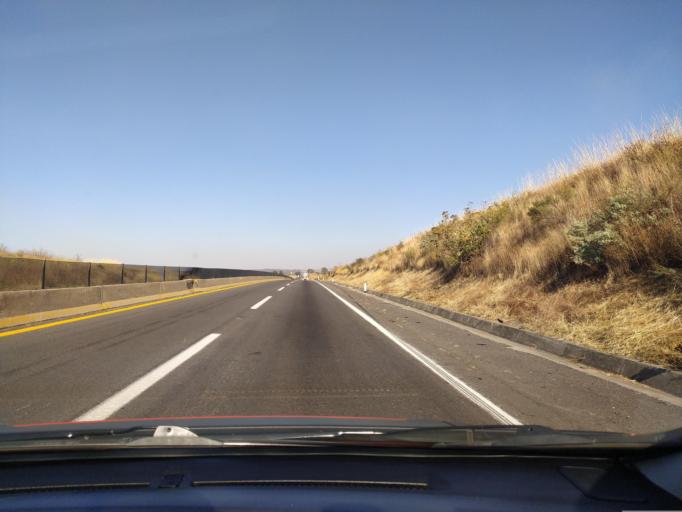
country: MX
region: Jalisco
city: Valle de Guadalupe
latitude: 20.9555
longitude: -102.6417
